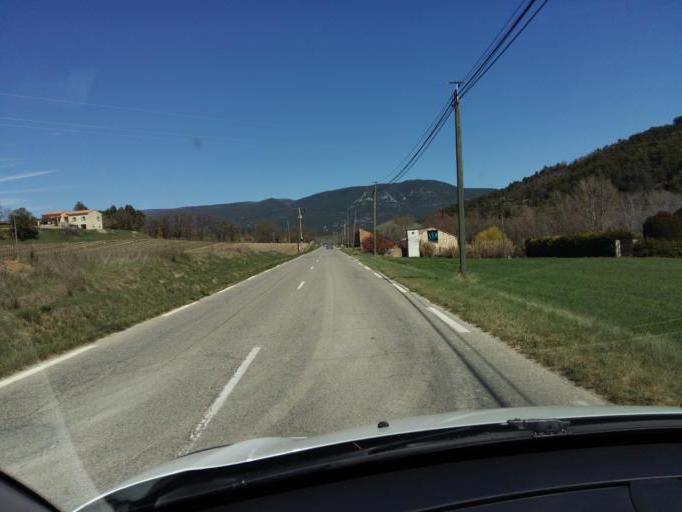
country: FR
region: Provence-Alpes-Cote d'Azur
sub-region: Departement du Vaucluse
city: Apt
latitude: 43.8965
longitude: 5.4314
